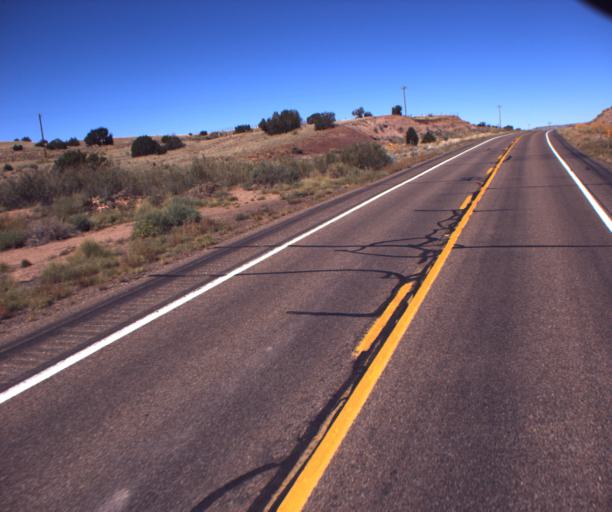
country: US
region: Arizona
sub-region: Apache County
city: Saint Johns
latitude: 34.4004
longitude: -109.4102
